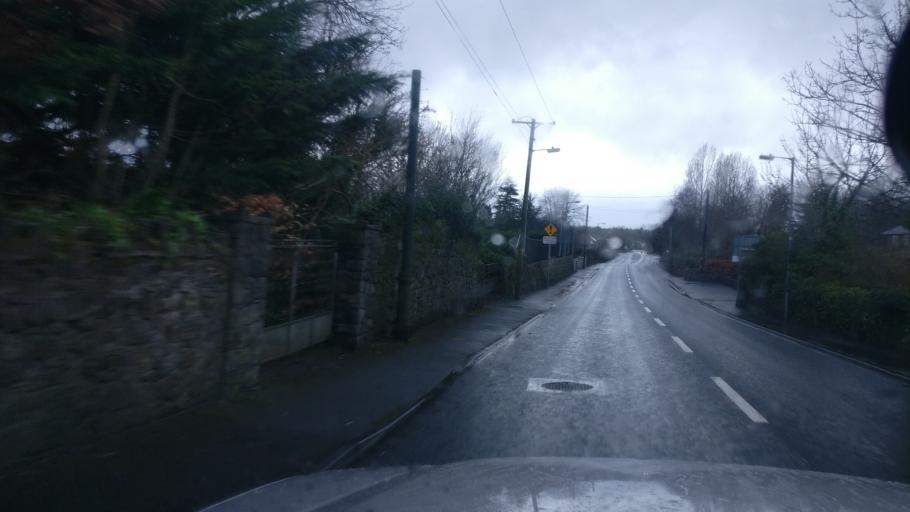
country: IE
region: Connaught
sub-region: County Galway
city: Portumna
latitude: 53.0909
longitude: -8.2259
